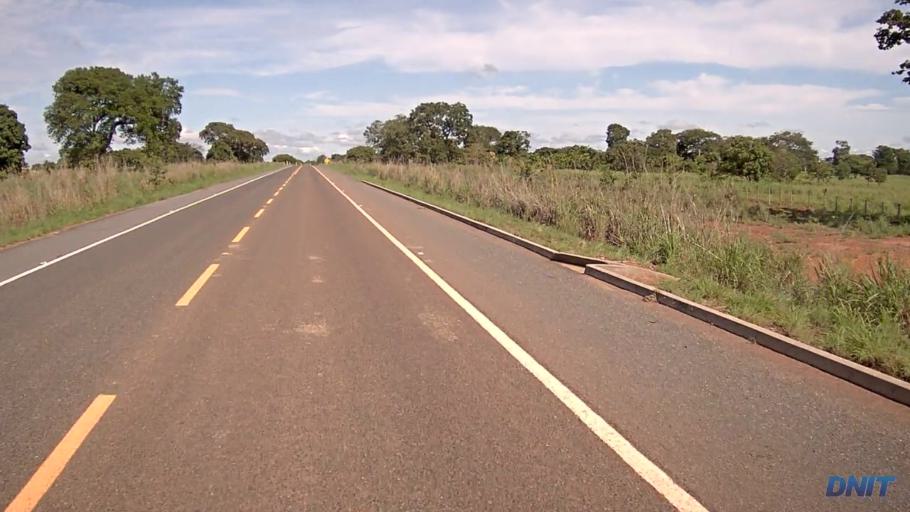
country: BR
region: Goias
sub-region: Sao Miguel Do Araguaia
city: Sao Miguel do Araguaia
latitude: -13.3181
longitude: -50.1639
